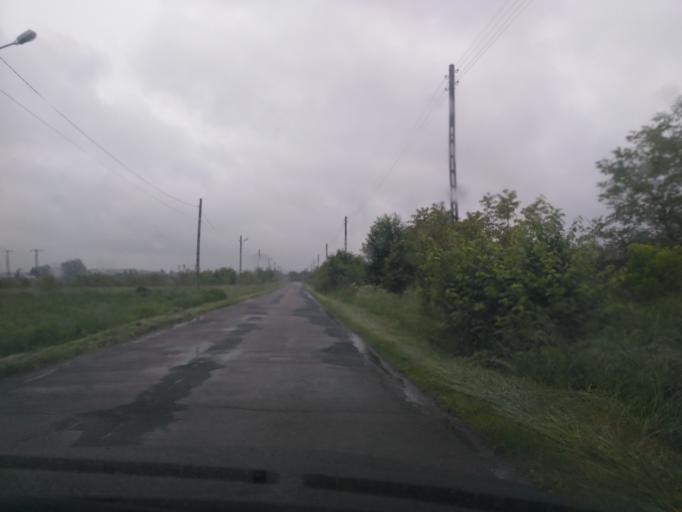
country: PL
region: Subcarpathian Voivodeship
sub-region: Powiat jasielski
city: Jaslo
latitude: 49.7444
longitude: 21.5039
